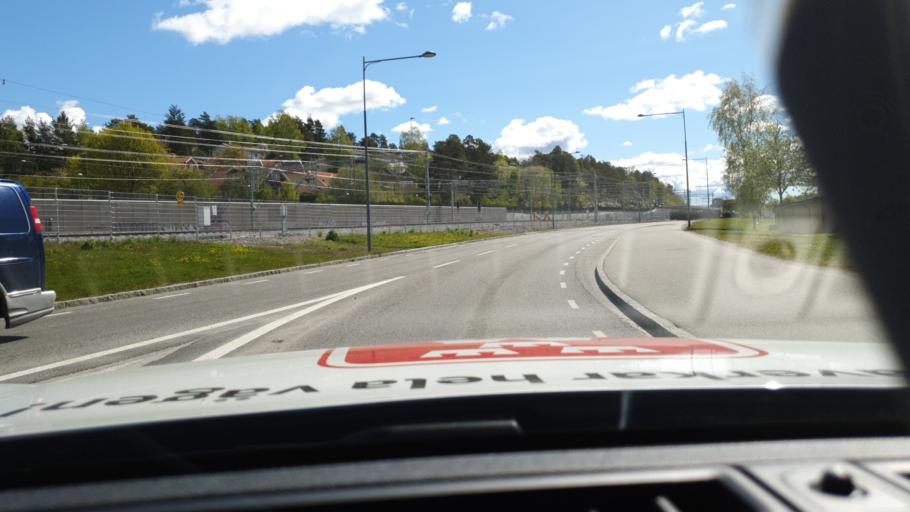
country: SE
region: Stockholm
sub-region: Stockholms Kommun
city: Kista
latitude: 59.3860
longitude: 17.8922
